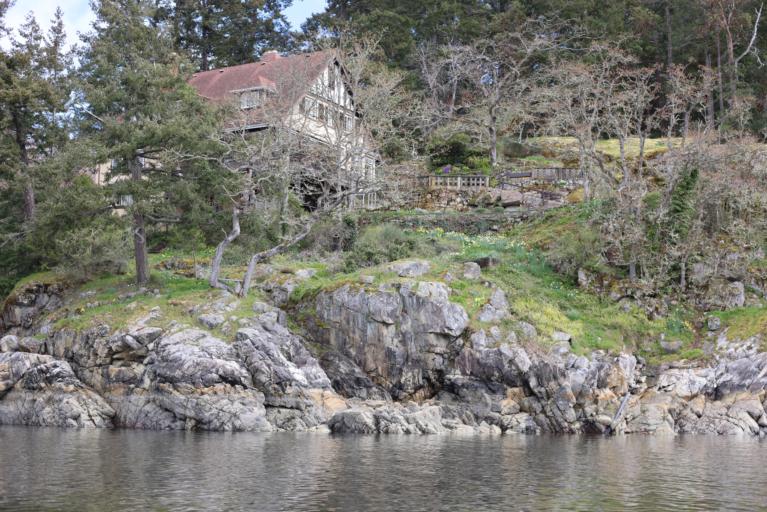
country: CA
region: British Columbia
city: North Saanich
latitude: 48.6066
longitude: -123.4818
